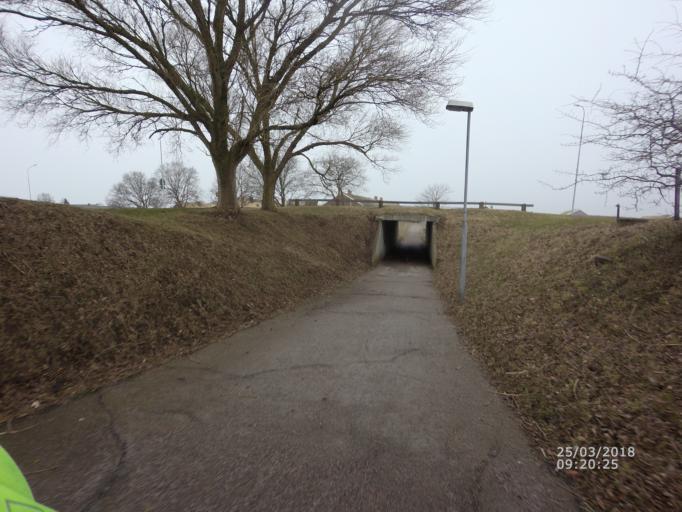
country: SE
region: Skane
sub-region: Hoganas Kommun
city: Hoganas
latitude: 56.1538
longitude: 12.5760
